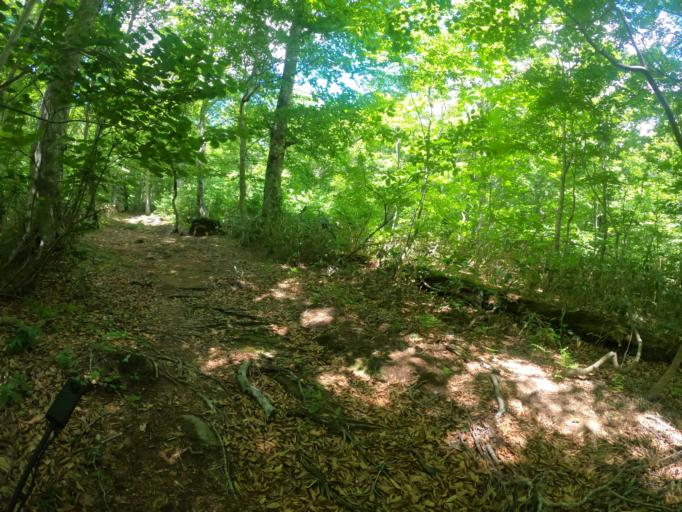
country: JP
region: Iwate
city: Ichinoseki
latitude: 38.9209
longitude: 140.8017
